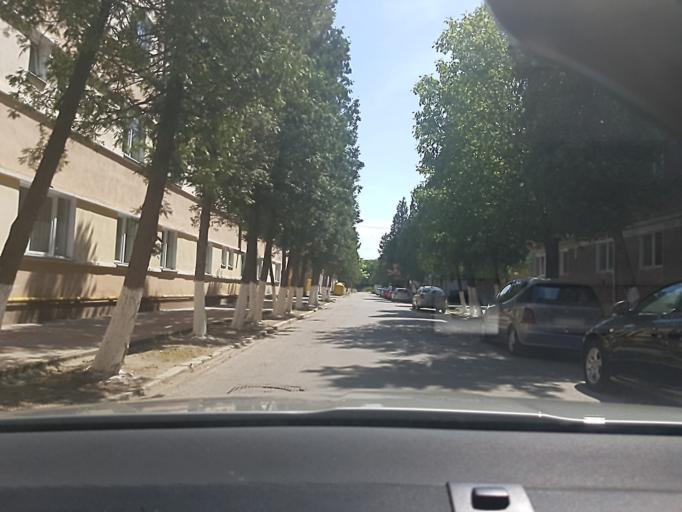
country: RO
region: Hunedoara
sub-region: Comuna Calan
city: Calan
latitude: 45.7316
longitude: 23.0281
